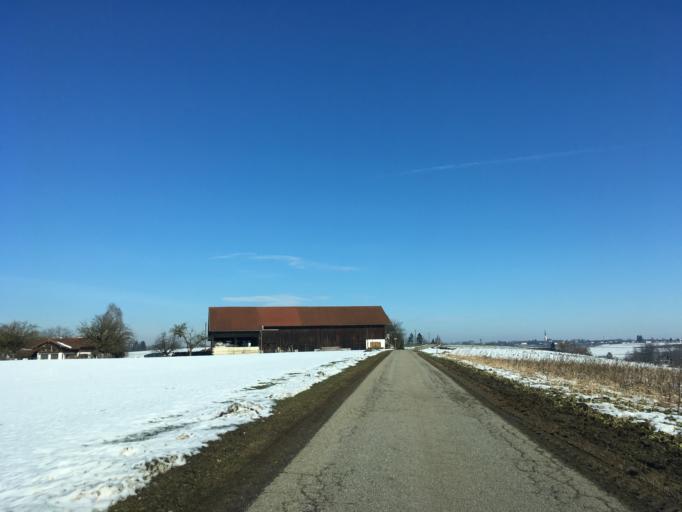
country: DE
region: Bavaria
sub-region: Upper Bavaria
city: Griesstatt
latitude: 47.9745
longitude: 12.1590
